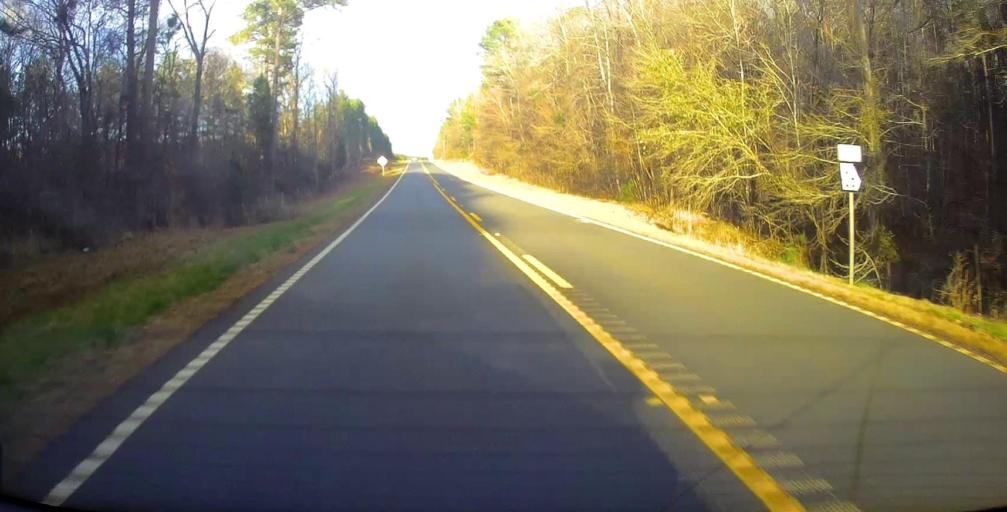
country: US
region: Georgia
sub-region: Talbot County
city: Sardis
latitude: 32.7450
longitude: -84.5961
